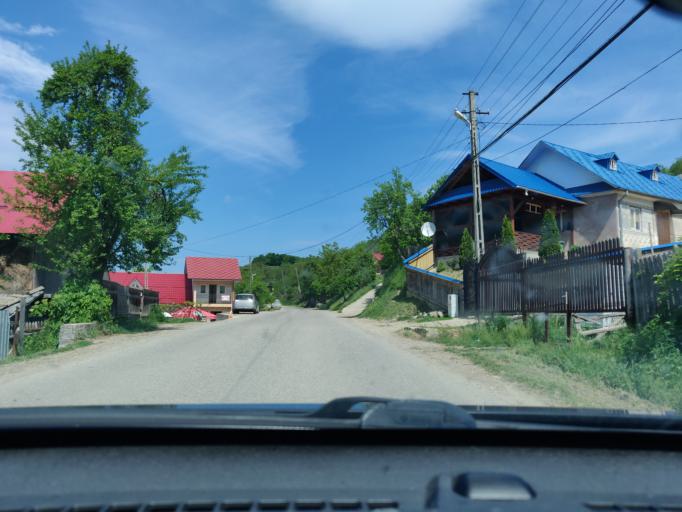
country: RO
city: Vizantea-Manastireasca
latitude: 45.9574
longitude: 26.8287
